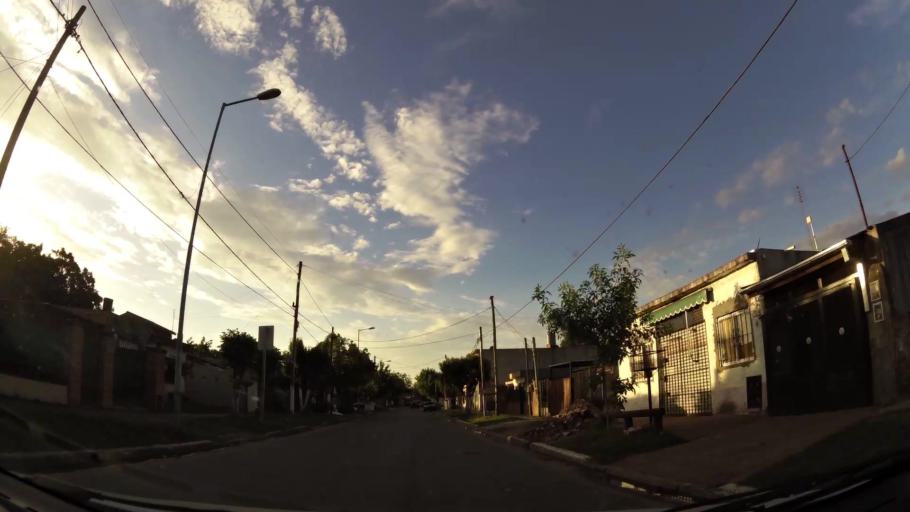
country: AR
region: Buenos Aires
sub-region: Partido de Merlo
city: Merlo
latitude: -34.6768
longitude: -58.7521
